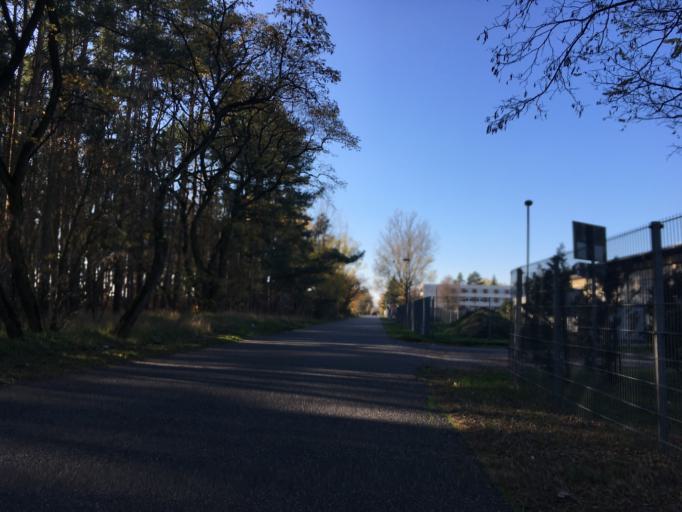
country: DE
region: Brandenburg
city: Spreenhagen
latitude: 52.3410
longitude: 13.8975
